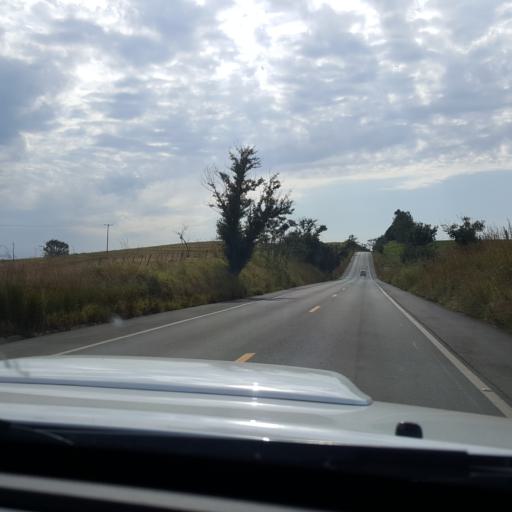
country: BR
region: Sao Paulo
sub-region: Itaporanga
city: Itaporanga
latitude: -23.7544
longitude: -49.4515
